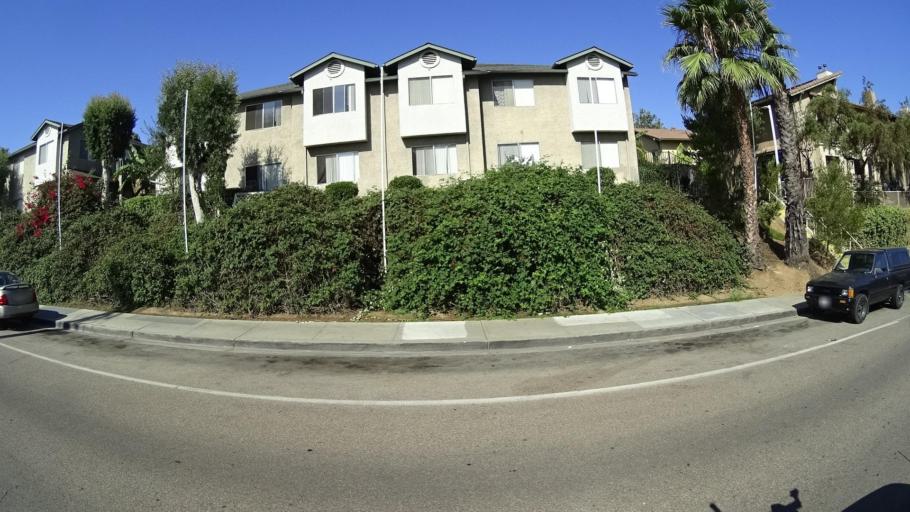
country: US
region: California
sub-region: San Diego County
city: Fallbrook
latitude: 33.3748
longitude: -117.2580
